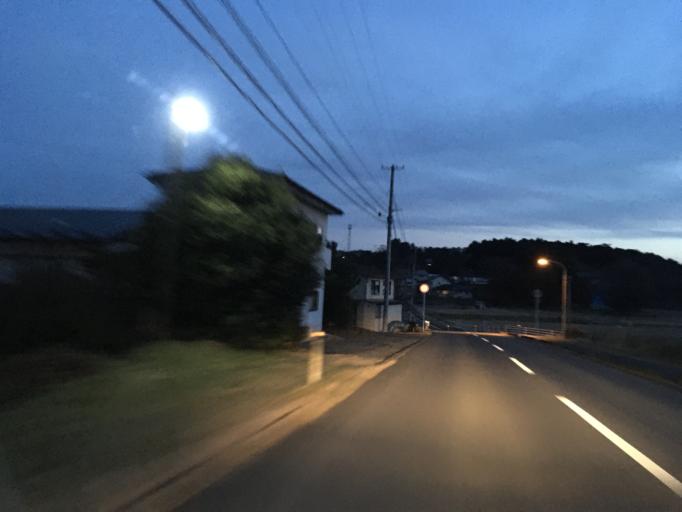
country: JP
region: Miyagi
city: Wakuya
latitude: 38.6988
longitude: 141.1604
